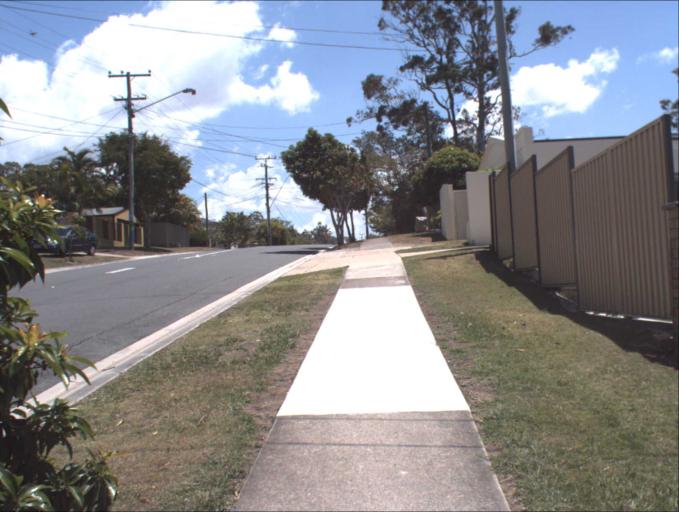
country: AU
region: Queensland
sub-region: Logan
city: Rochedale South
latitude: -27.5990
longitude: 153.1350
